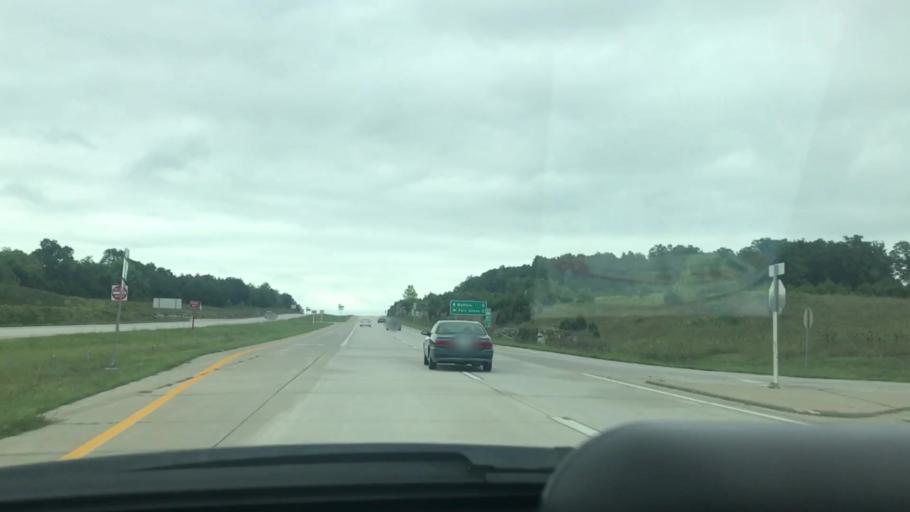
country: US
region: Missouri
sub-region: Greene County
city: Fair Grove
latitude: 37.5173
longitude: -93.1382
